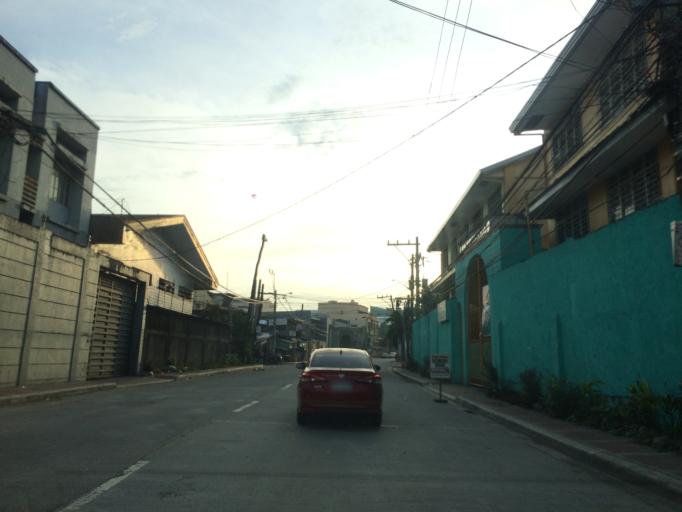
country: PH
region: Calabarzon
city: Del Monte
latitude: 14.6404
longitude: 120.9936
